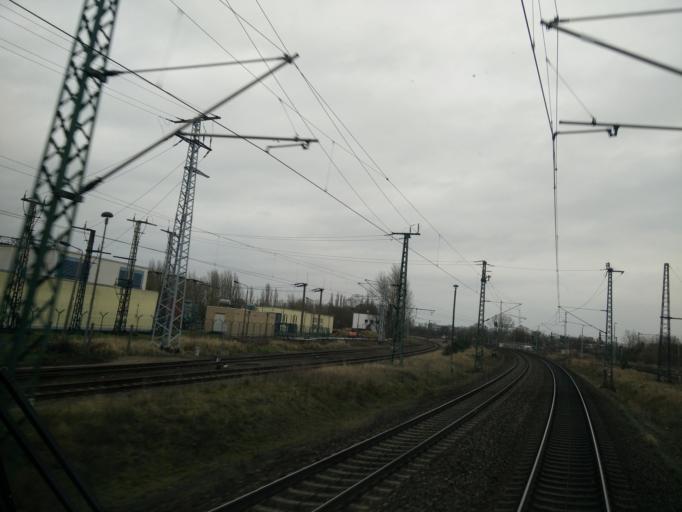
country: DE
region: Brandenburg
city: Wittenberge
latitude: 52.9964
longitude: 11.7677
